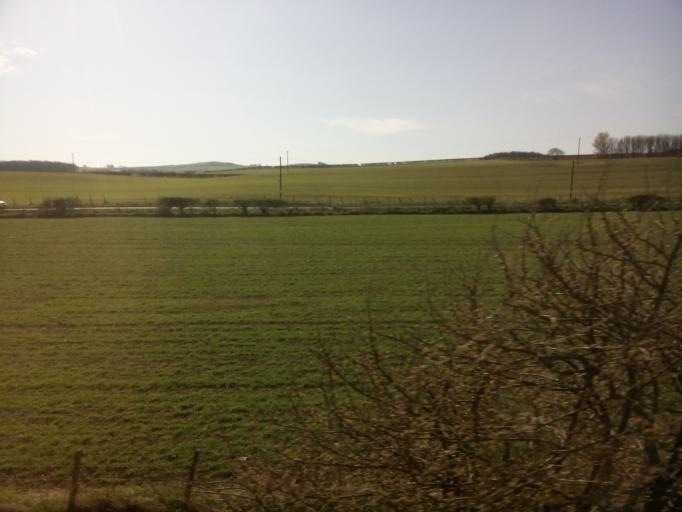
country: GB
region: Scotland
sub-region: East Lothian
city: Gullane
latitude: 55.9885
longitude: -2.8409
